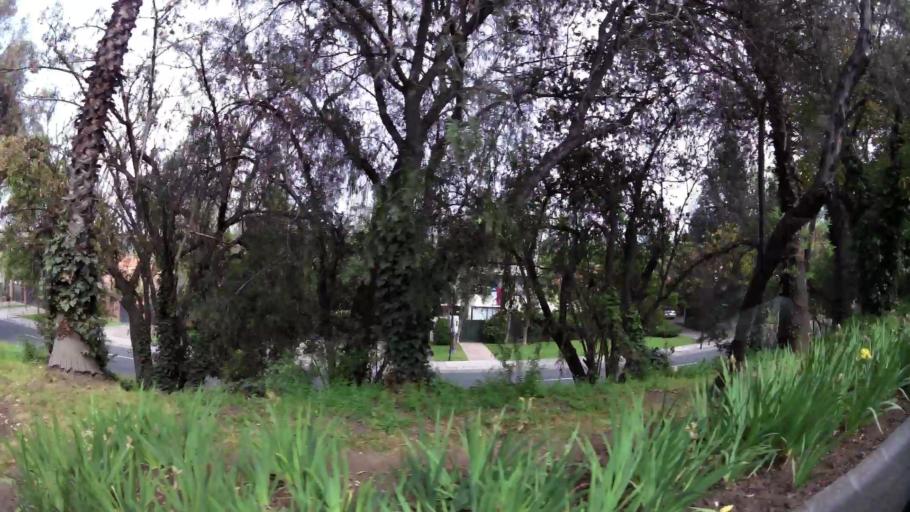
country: CL
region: Santiago Metropolitan
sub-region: Provincia de Santiago
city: Villa Presidente Frei, Nunoa, Santiago, Chile
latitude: -33.3720
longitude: -70.5715
